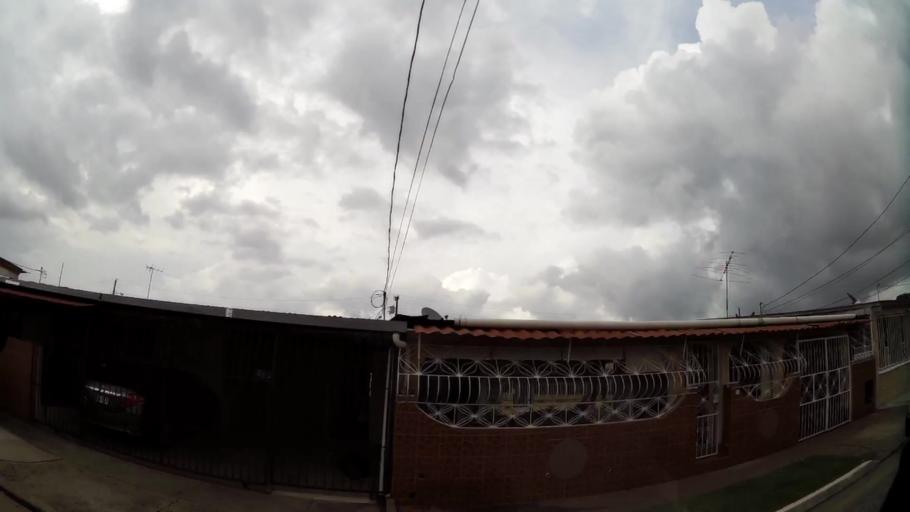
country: PA
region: Panama
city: Tocumen
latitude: 9.0594
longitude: -79.4128
